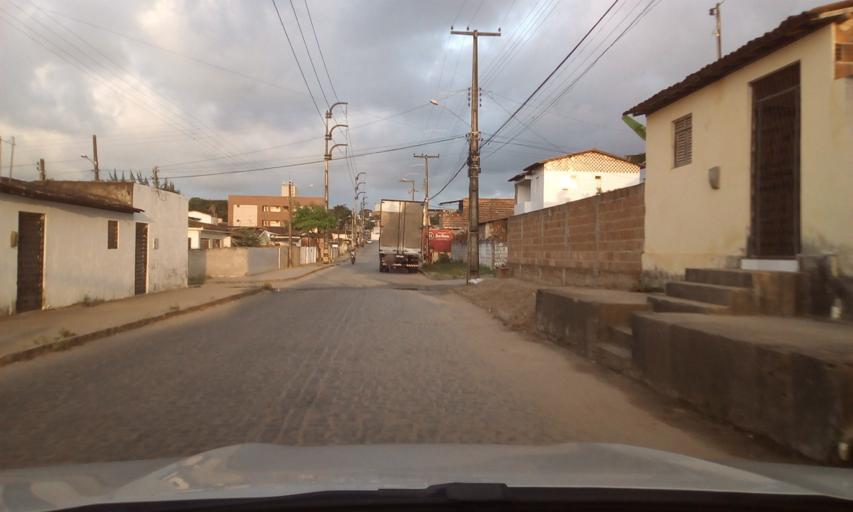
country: BR
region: Paraiba
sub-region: Bayeux
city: Bayeux
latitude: -7.1843
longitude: -34.8896
